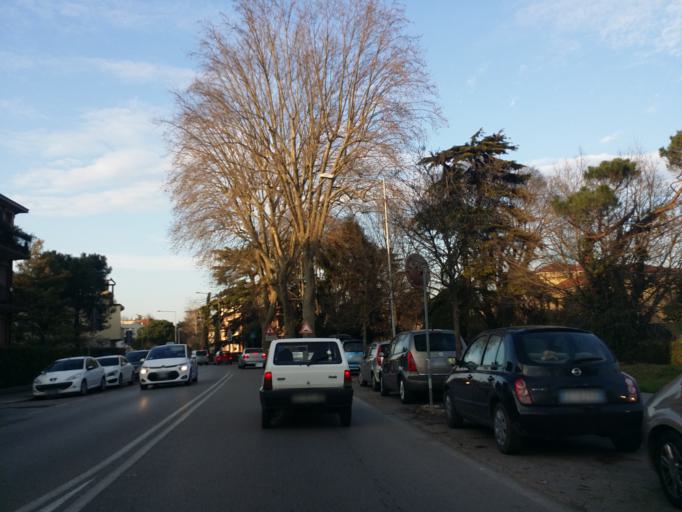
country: IT
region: Veneto
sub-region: Provincia di Padova
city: Padova
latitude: 45.4021
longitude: 11.8637
